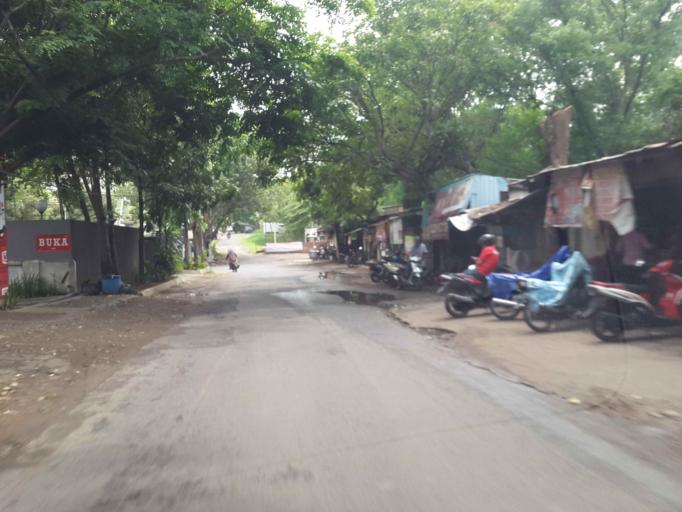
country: ID
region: Central Java
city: Semarang
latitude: -7.0140
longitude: 110.4121
